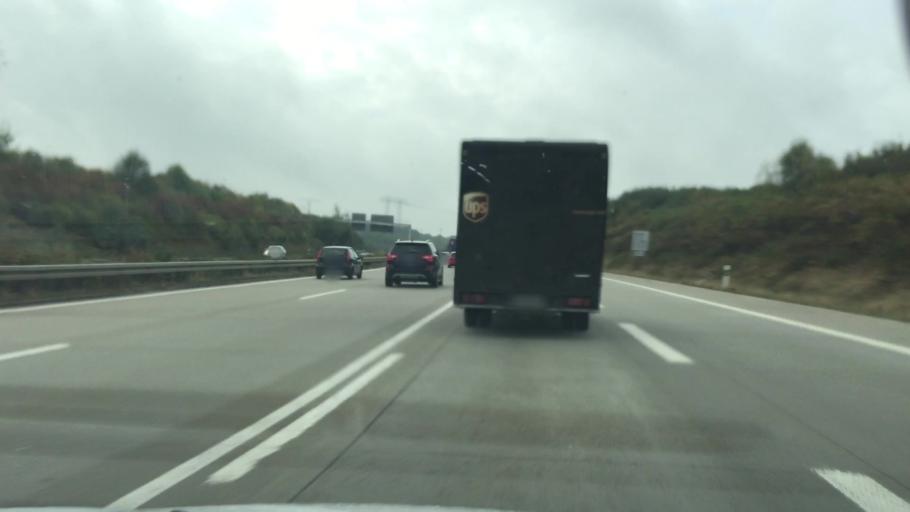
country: DE
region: Saxony
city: Wittgensdorf
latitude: 50.8545
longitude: 12.8349
